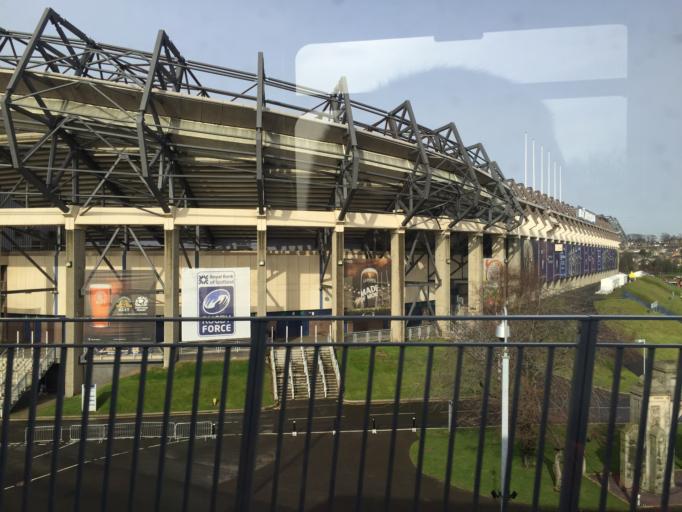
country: GB
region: Scotland
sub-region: Edinburgh
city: Colinton
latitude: 55.9413
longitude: -3.2388
